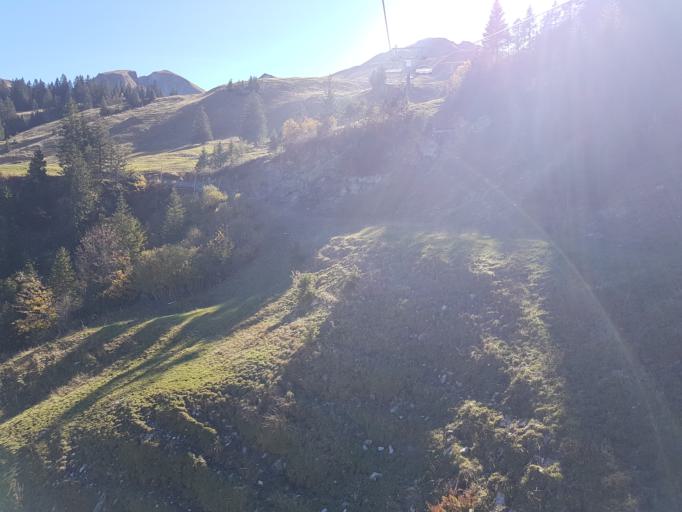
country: CH
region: Schwyz
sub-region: Bezirk Schwyz
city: Ibach
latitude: 46.9700
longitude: 8.6723
